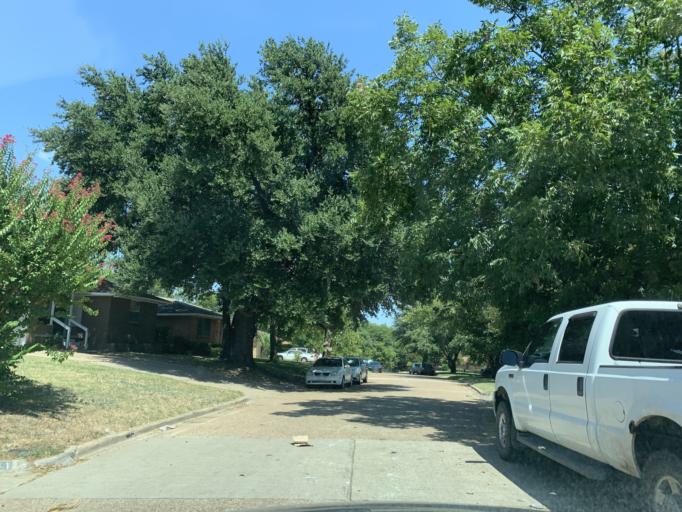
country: US
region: Texas
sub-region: Dallas County
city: Cockrell Hill
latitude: 32.6781
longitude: -96.8075
